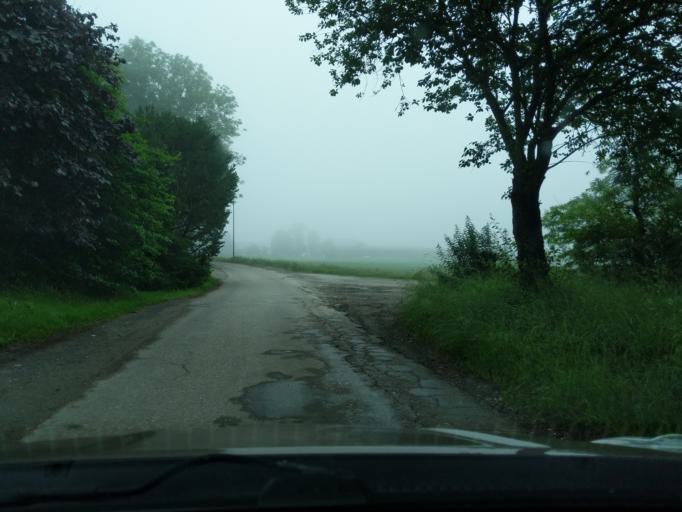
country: DE
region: Bavaria
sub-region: Swabia
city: Gessertshausen
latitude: 48.3301
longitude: 10.7425
